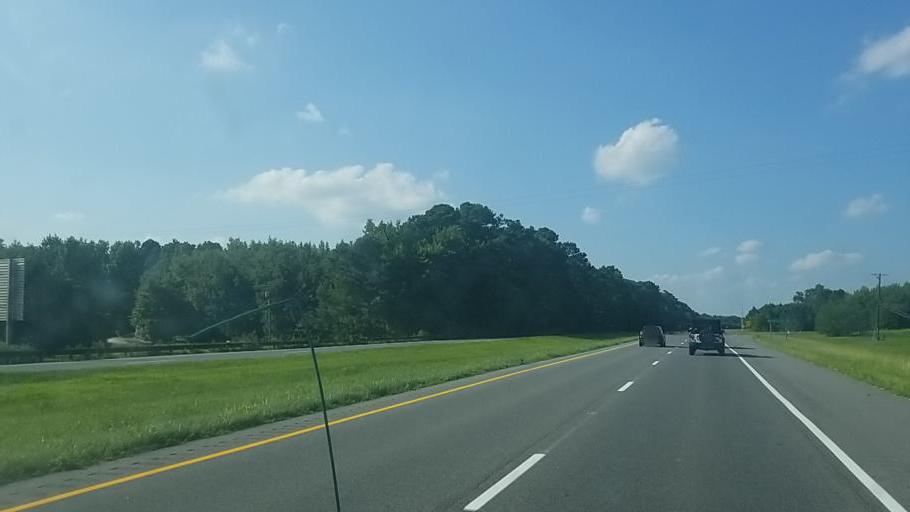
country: US
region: Maryland
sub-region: Worcester County
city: Berlin
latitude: 38.3551
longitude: -75.2140
